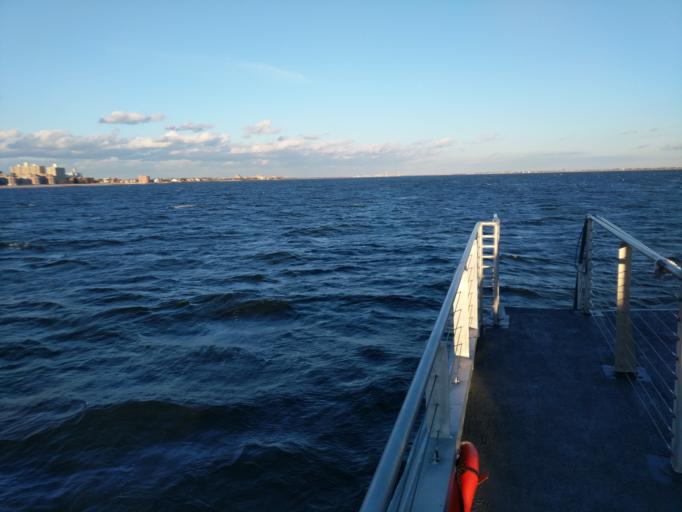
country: US
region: New York
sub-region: Kings County
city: Coney Island
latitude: 40.5660
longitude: -73.9712
